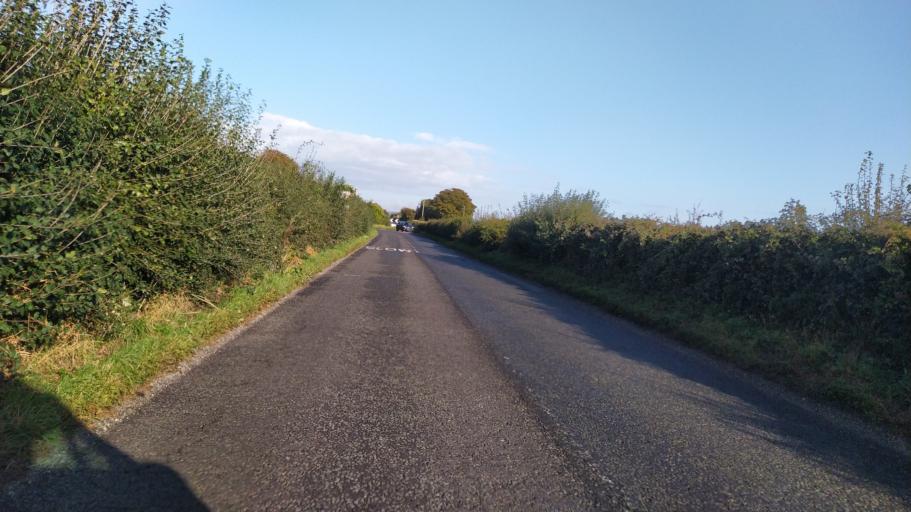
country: GB
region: England
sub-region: Wiltshire
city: Bower Chalke
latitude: 50.9154
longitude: -2.0490
